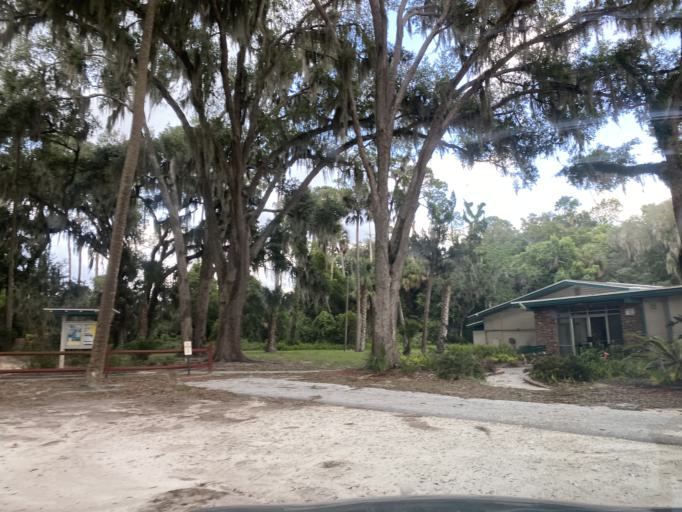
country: US
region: Florida
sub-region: Volusia County
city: Deltona
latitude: 28.8631
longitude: -81.2519
